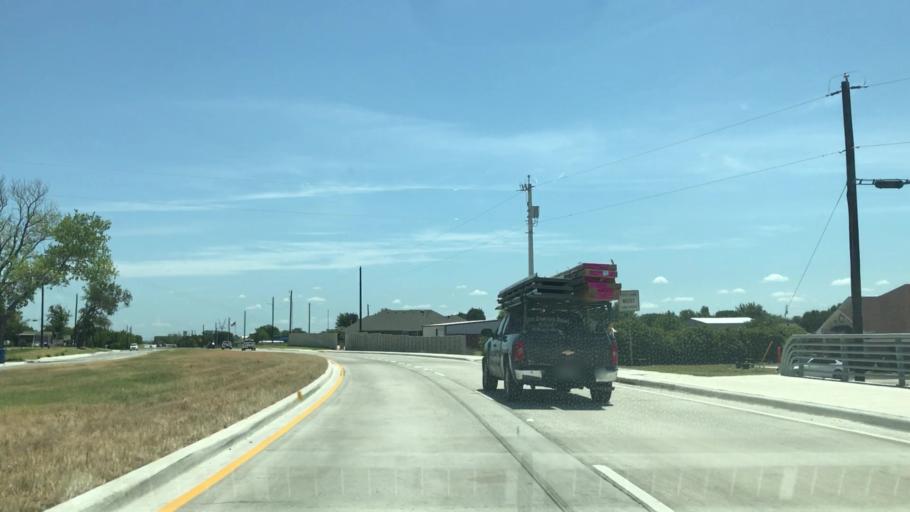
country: US
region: Texas
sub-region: Collin County
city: Saint Paul
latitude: 33.0516
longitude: -96.5629
